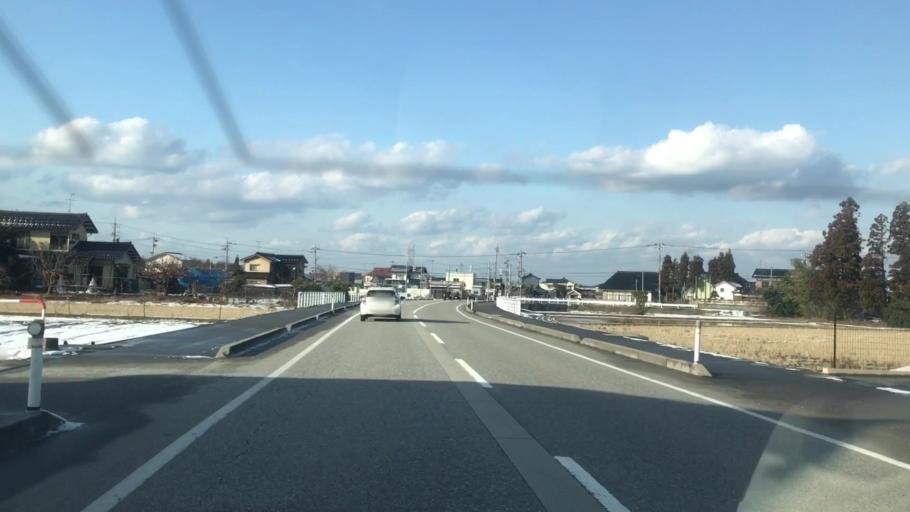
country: JP
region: Toyama
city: Toyama-shi
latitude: 36.6739
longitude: 137.2744
